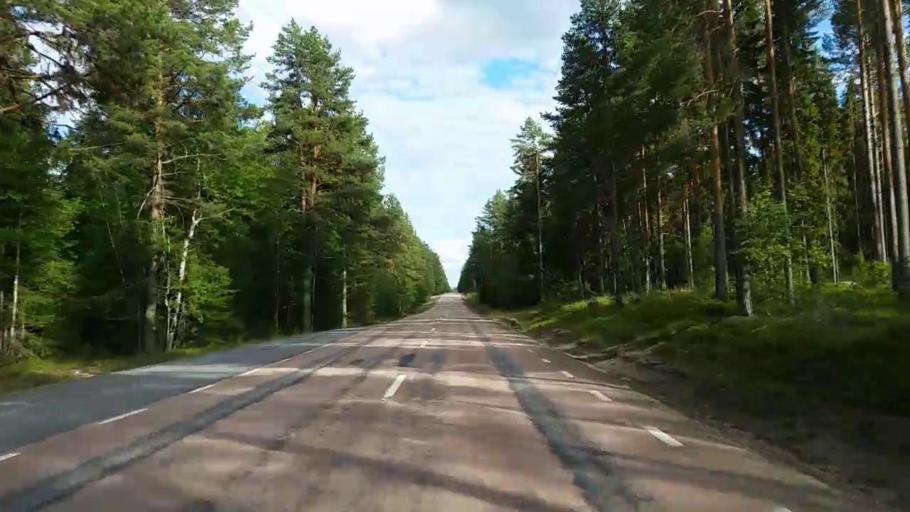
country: SE
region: Gaevleborg
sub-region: Ljusdals Kommun
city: Farila
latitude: 61.8867
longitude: 15.9297
